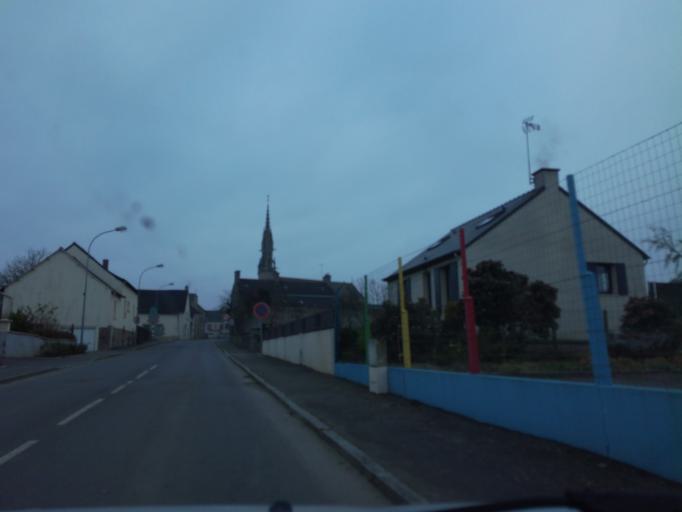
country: FR
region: Brittany
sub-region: Departement d'Ille-et-Vilaine
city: Gosne
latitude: 48.2471
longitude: -1.4619
